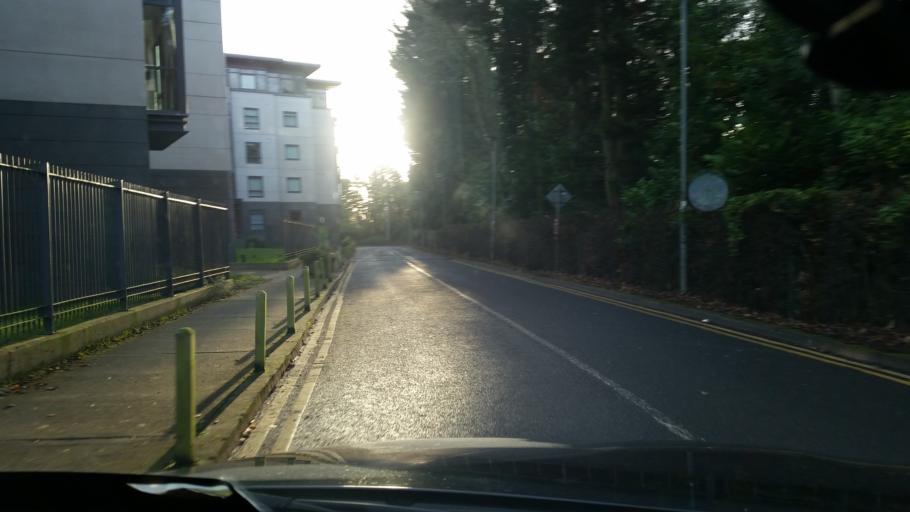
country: IE
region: Leinster
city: Glasnevin
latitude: 53.3835
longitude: -6.2589
